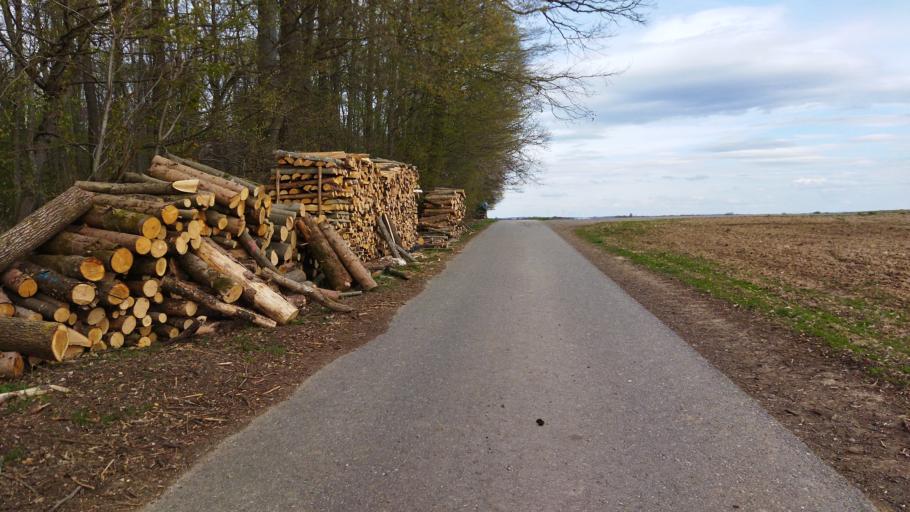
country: DE
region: Baden-Wuerttemberg
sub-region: Regierungsbezirk Stuttgart
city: Neudenau
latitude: 49.3018
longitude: 9.2211
